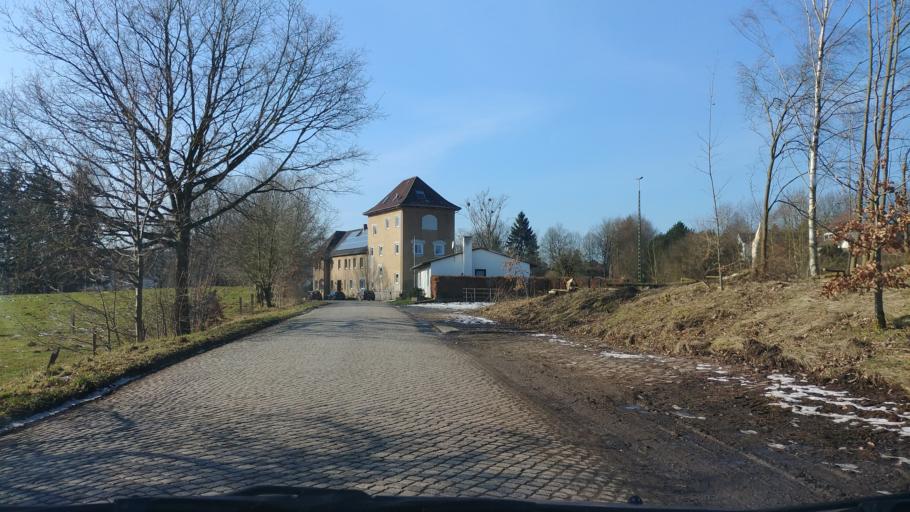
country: DE
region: Lower Saxony
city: Uslar
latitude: 51.6539
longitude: 9.6539
